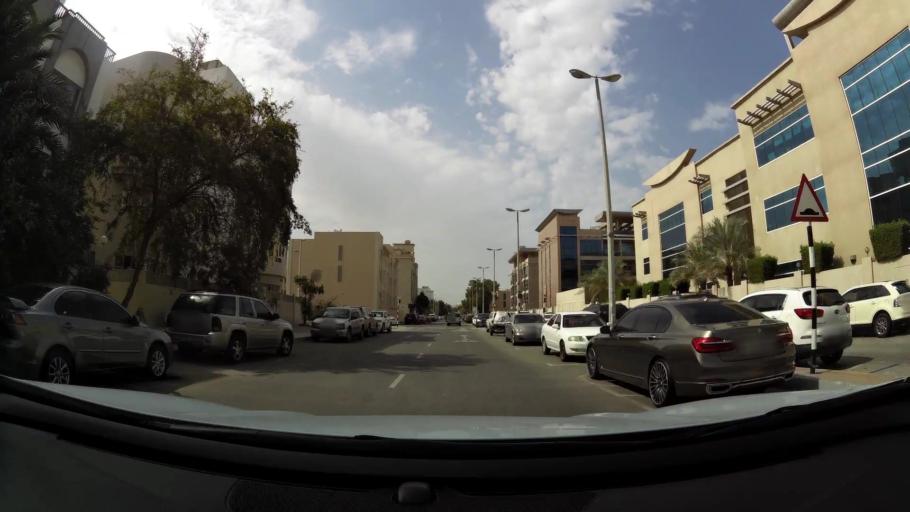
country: AE
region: Abu Dhabi
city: Abu Dhabi
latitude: 24.4560
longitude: 54.3603
